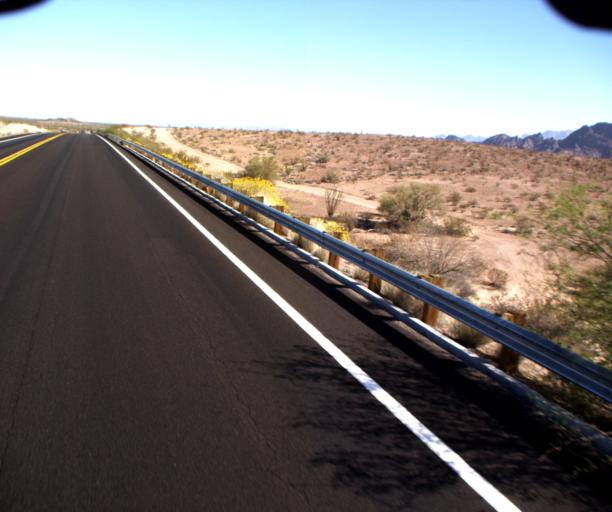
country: US
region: Arizona
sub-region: La Paz County
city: Quartzsite
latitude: 33.2447
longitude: -114.2480
